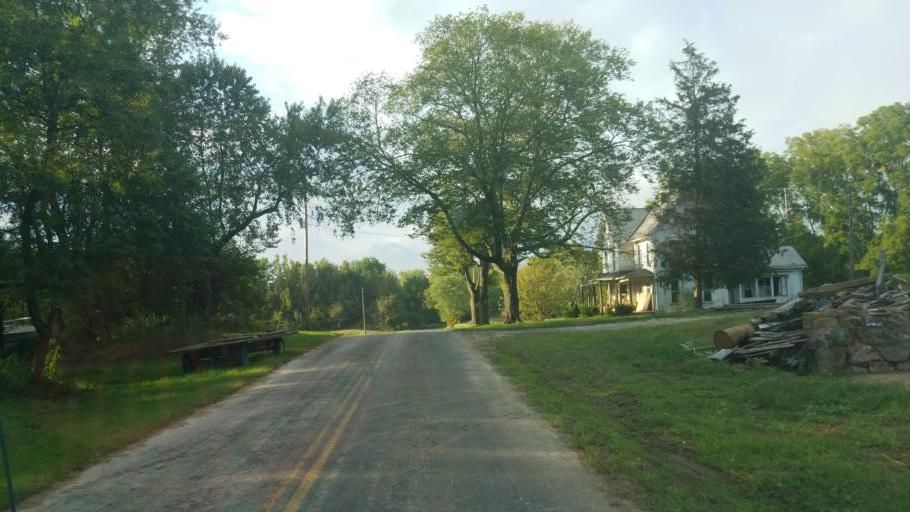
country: US
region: Ohio
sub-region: Wayne County
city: Shreve
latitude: 40.7455
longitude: -82.1314
